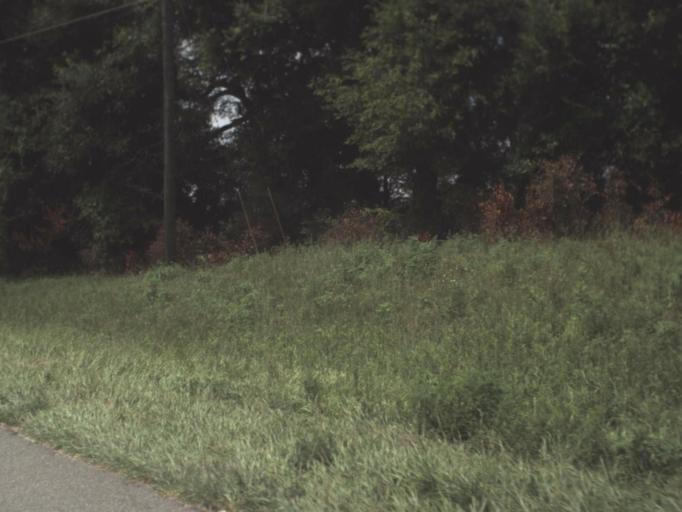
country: US
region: Florida
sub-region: Gilchrist County
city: Trenton
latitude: 29.6832
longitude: -82.8573
